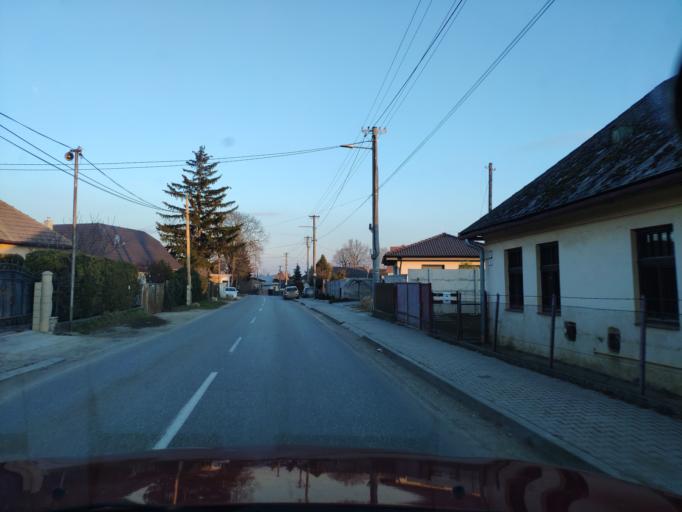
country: SK
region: Nitriansky
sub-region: Okres Nitra
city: Nitra
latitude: 48.2114
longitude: 18.0602
